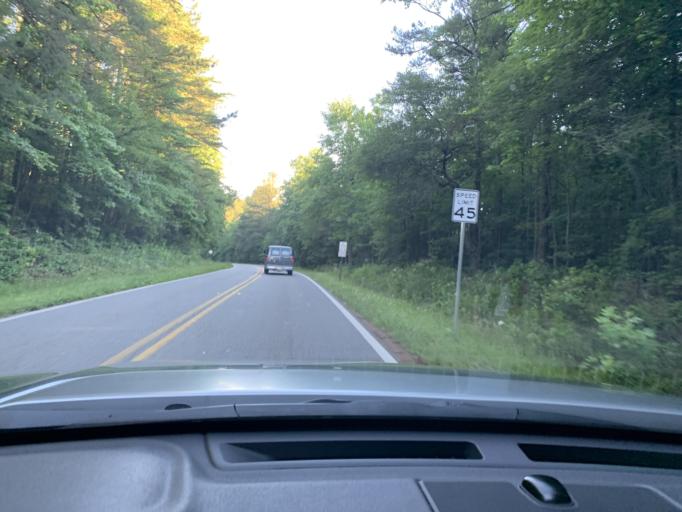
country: US
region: Georgia
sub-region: Bartow County
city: Rydal
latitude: 34.2670
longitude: -84.7108
